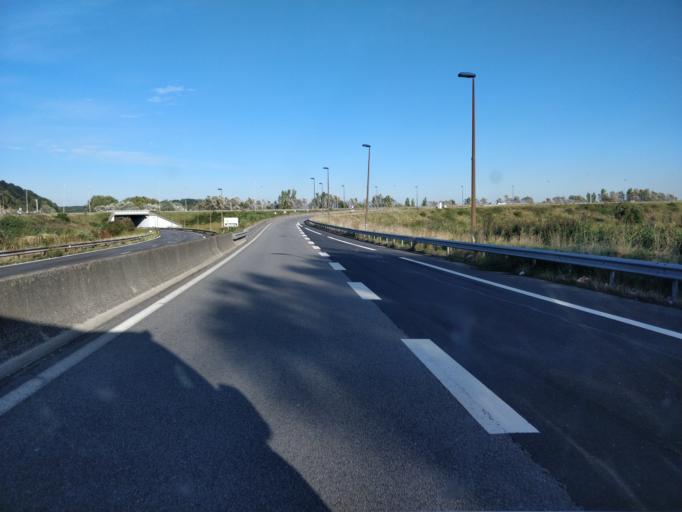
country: FR
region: Haute-Normandie
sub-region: Departement de la Seine-Maritime
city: Rogerville
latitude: 49.4931
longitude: 0.2625
